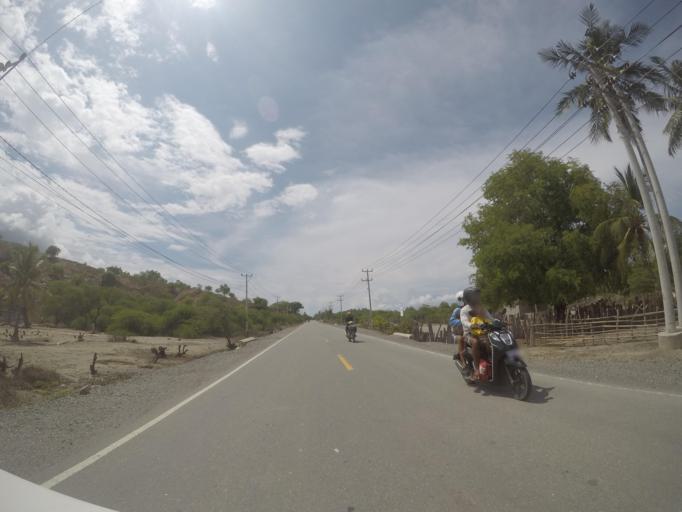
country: TL
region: Liquica
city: Liquica
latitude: -8.5668
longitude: 125.4282
